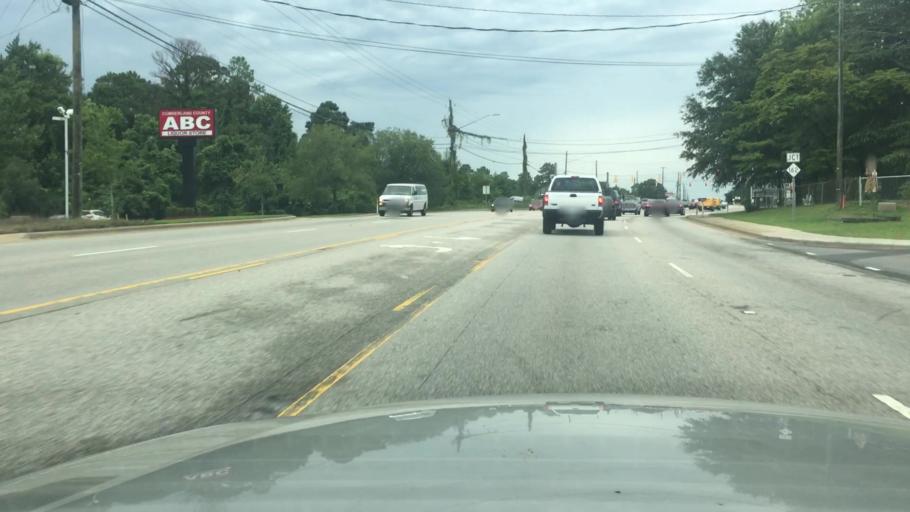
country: US
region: North Carolina
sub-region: Cumberland County
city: Hope Mills
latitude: 34.9936
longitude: -78.9678
